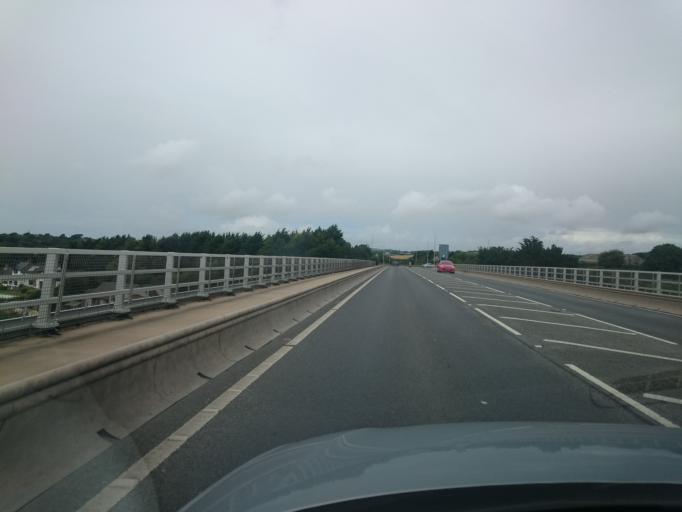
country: GB
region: Wales
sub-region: Pembrokeshire
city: Burton
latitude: 51.7092
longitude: -4.9351
